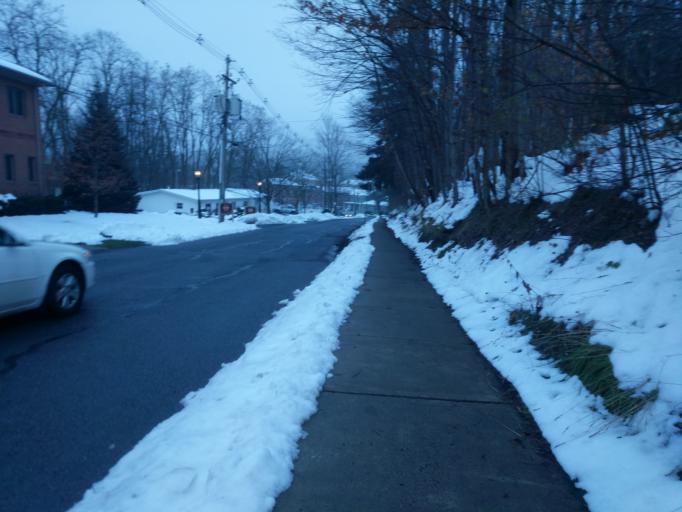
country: US
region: Pennsylvania
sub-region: Tioga County
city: Wellsboro
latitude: 41.7499
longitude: -77.3032
